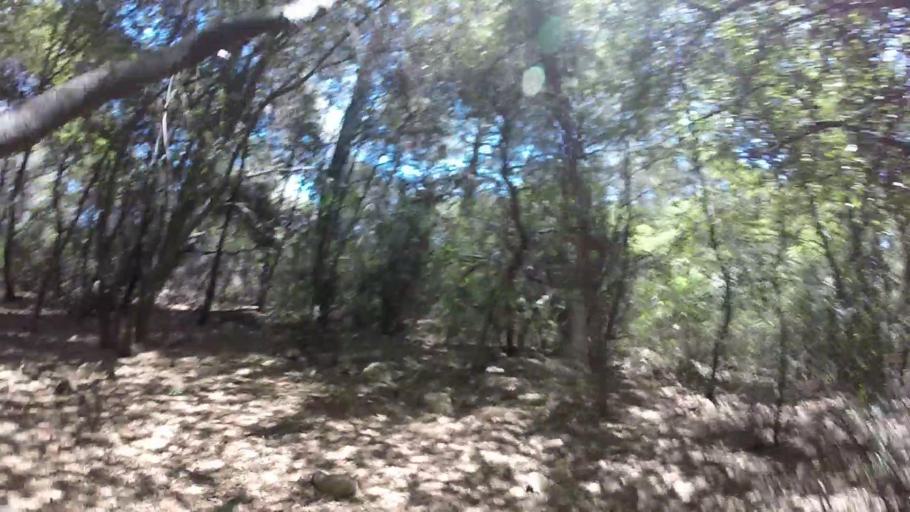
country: FR
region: Provence-Alpes-Cote d'Azur
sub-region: Departement des Alpes-Maritimes
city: Vallauris
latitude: 43.6085
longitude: 7.0393
